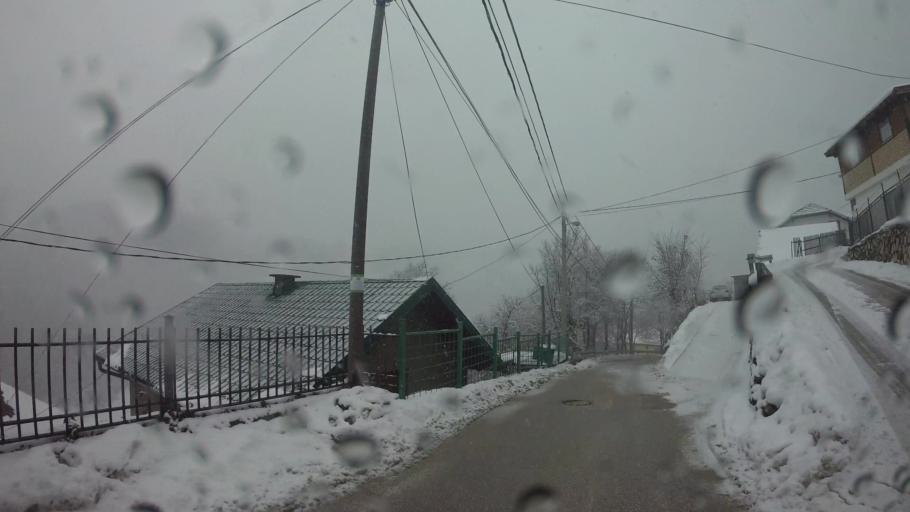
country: BA
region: Federation of Bosnia and Herzegovina
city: Kobilja Glava
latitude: 43.8522
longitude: 18.4510
